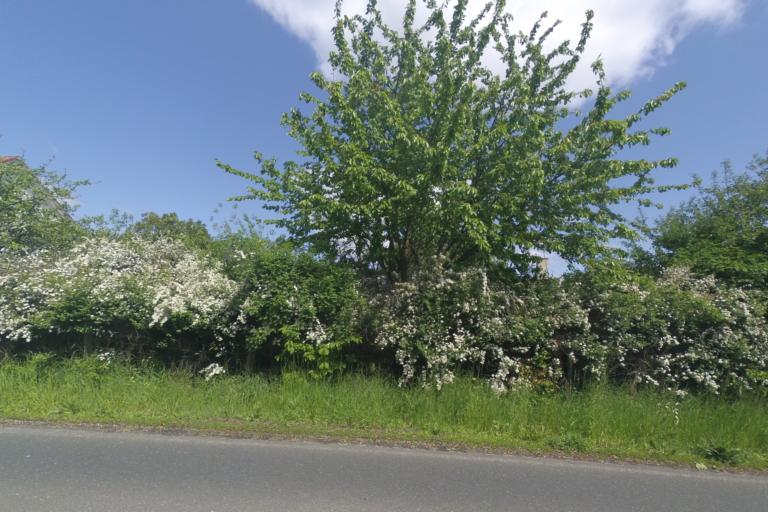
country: DE
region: Hesse
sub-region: Regierungsbezirk Darmstadt
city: Karben
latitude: 50.2415
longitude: 8.7245
